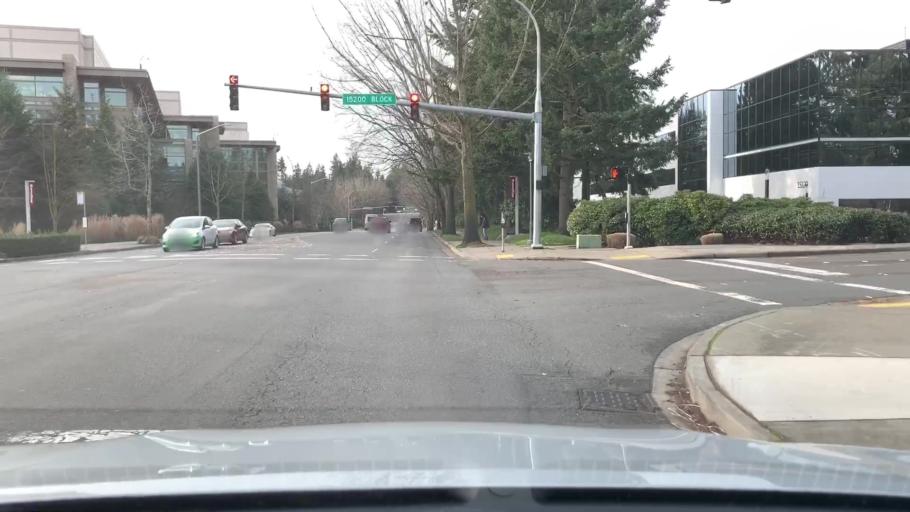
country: US
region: Washington
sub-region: King County
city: Redmond
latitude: 47.6461
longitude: -122.1373
